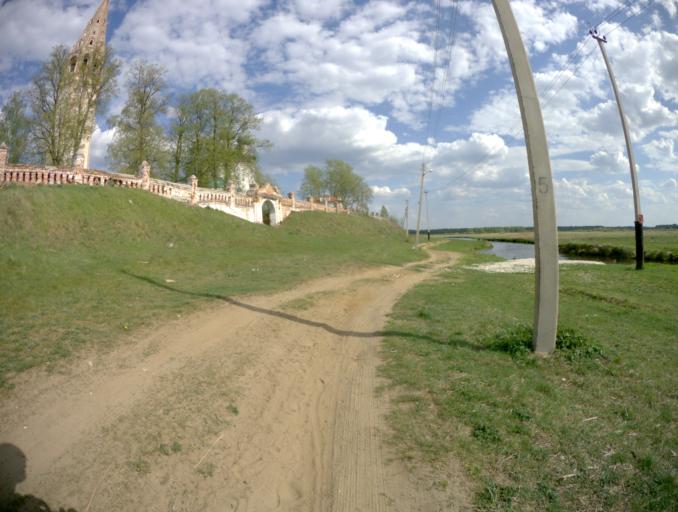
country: RU
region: Vladimir
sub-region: Kovrovskiy Rayon
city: Kovrov
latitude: 56.4447
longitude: 41.3287
